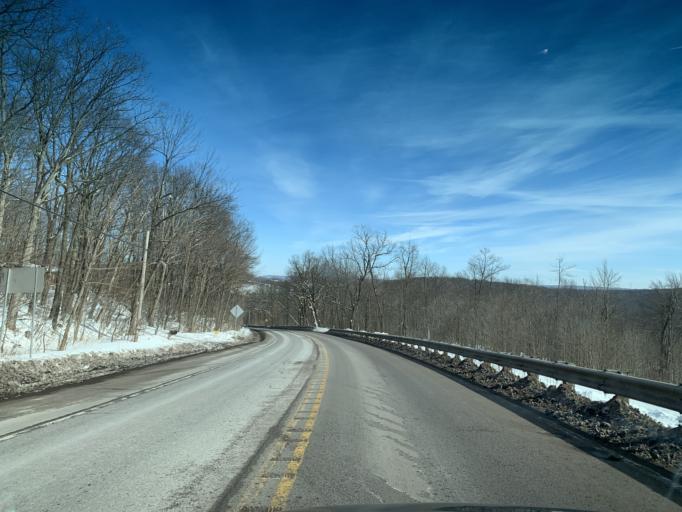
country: US
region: Pennsylvania
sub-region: Somerset County
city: Meyersdale
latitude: 39.6862
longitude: -79.0838
